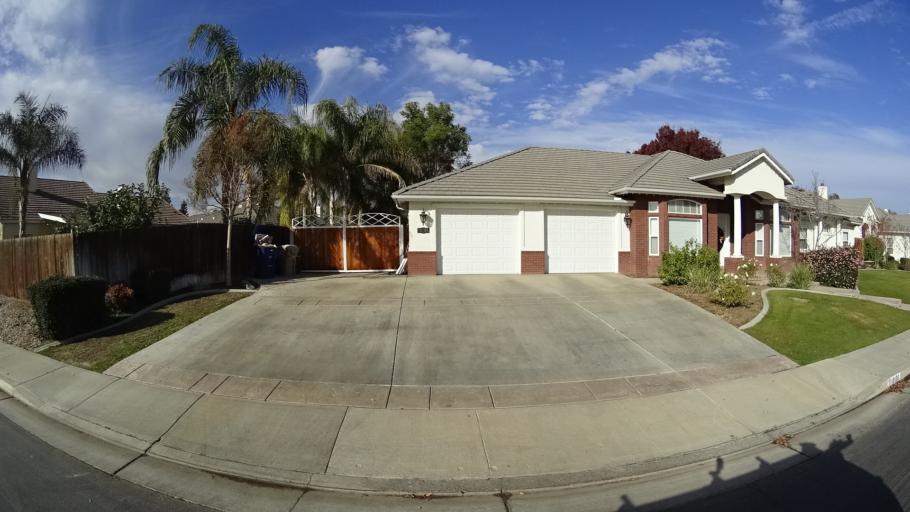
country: US
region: California
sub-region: Kern County
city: Greenacres
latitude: 35.4029
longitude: -119.1155
